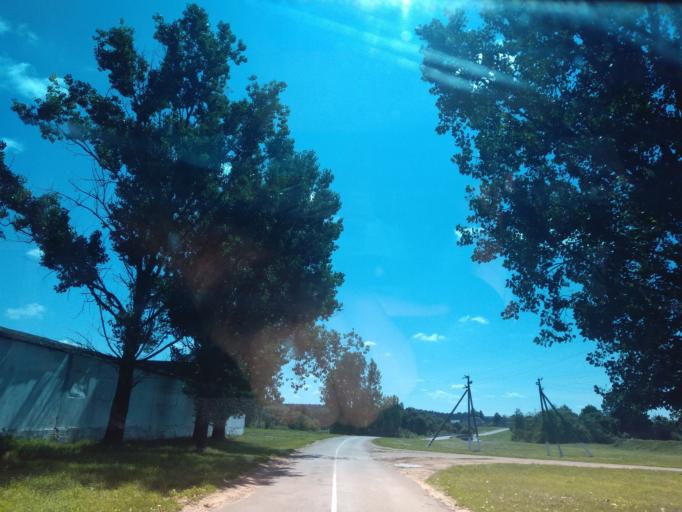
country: BY
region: Minsk
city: Kapyl'
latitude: 53.2567
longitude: 27.1827
